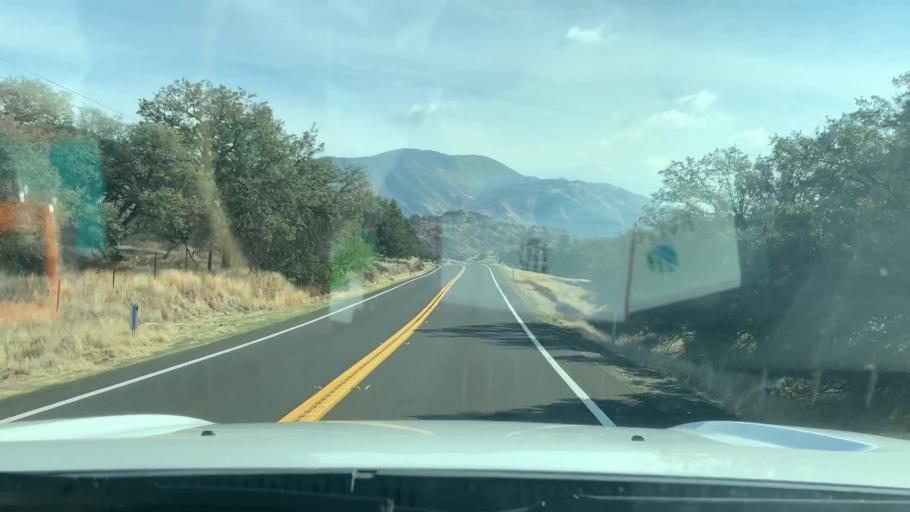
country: US
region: California
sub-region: Fresno County
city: Coalinga
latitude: 36.0884
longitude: -120.4961
